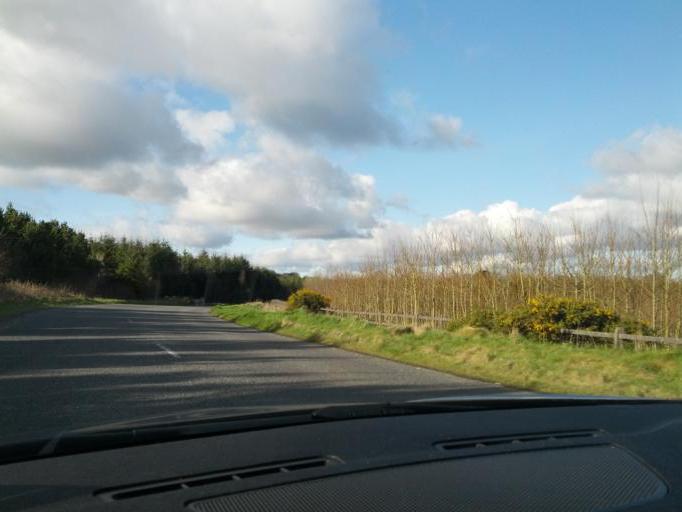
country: IE
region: Connaught
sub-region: Roscommon
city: Castlerea
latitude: 53.6196
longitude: -8.5510
